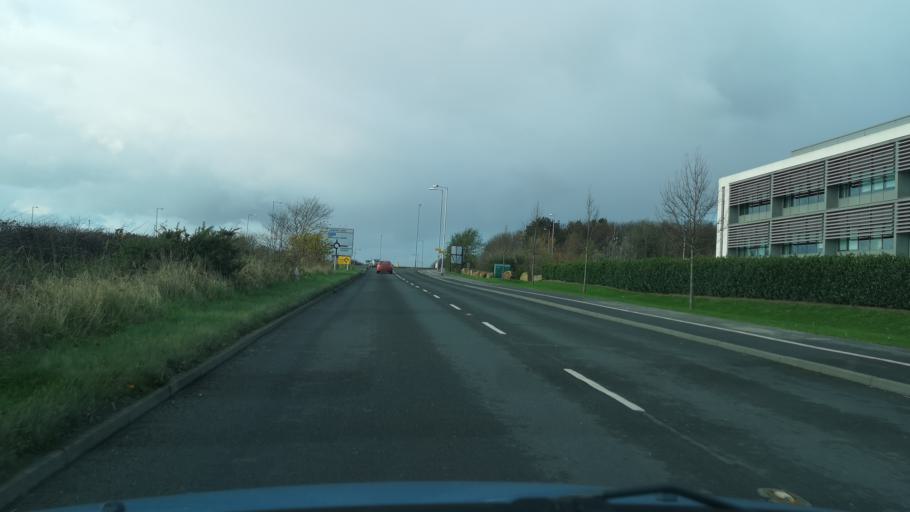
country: GB
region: England
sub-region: City and Borough of Wakefield
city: Normanton
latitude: 53.6985
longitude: -1.3880
